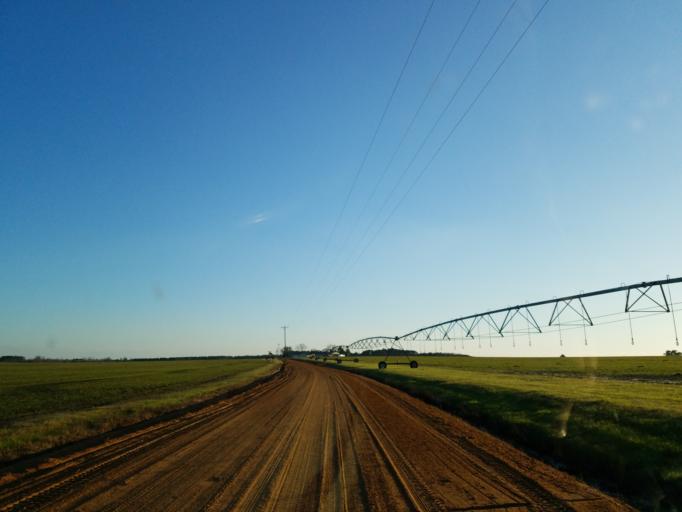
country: US
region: Georgia
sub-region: Worth County
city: Sylvester
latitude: 31.6089
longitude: -83.7867
